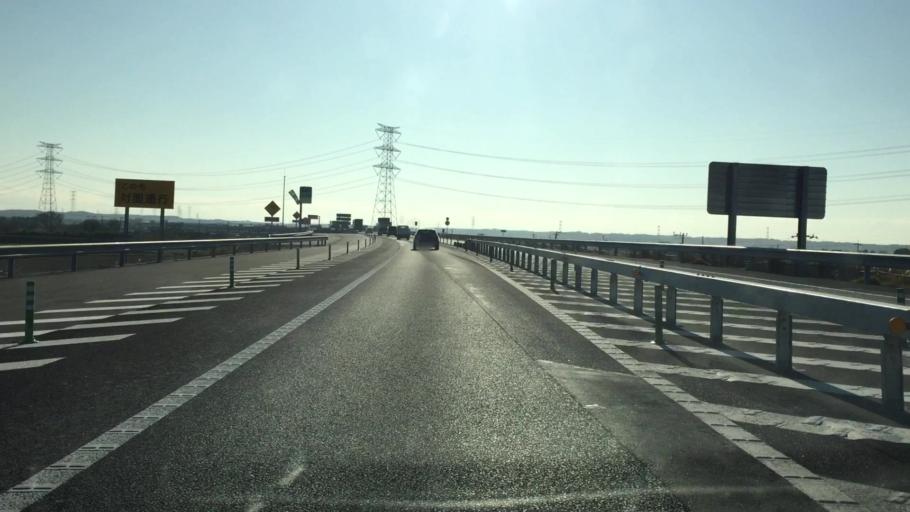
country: JP
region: Ibaraki
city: Inashiki
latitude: 35.9187
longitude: 140.3518
